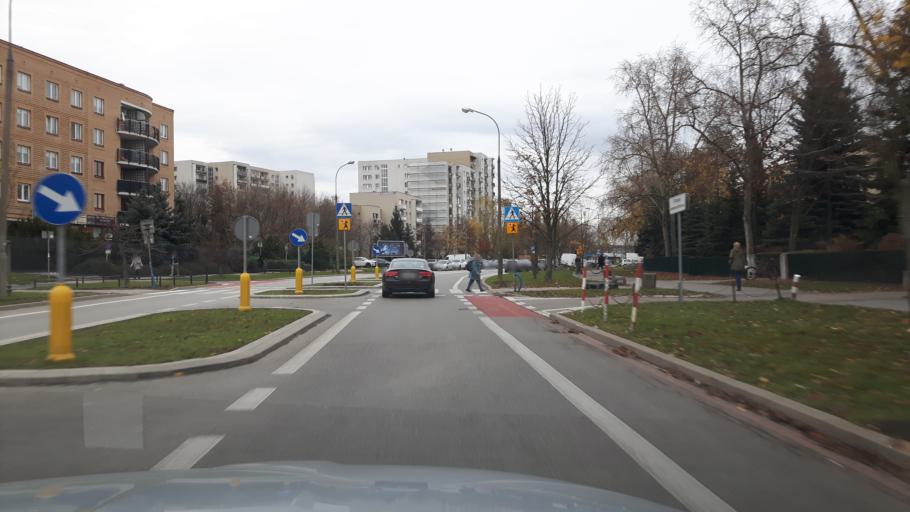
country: PL
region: Masovian Voivodeship
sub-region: Warszawa
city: Ursynow
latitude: 52.1499
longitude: 21.0536
